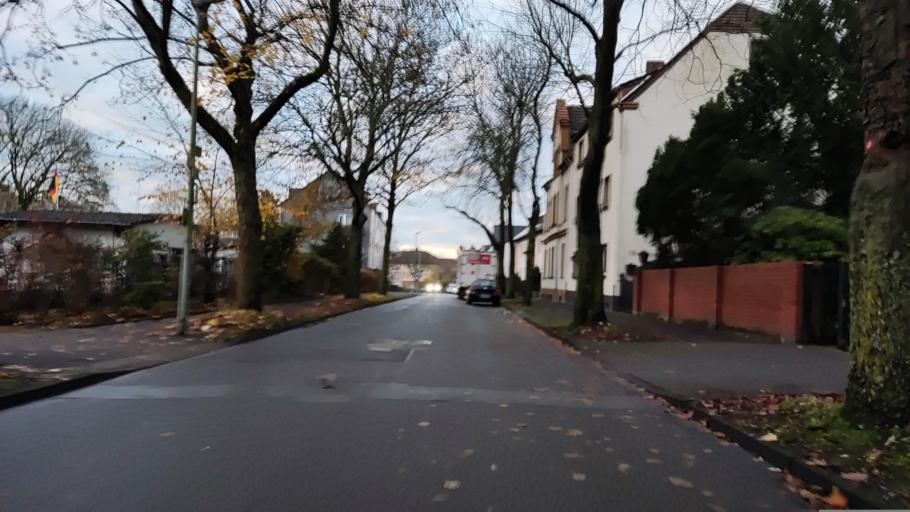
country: DE
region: North Rhine-Westphalia
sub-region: Regierungsbezirk Arnsberg
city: Herne
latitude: 51.5312
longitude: 7.1937
